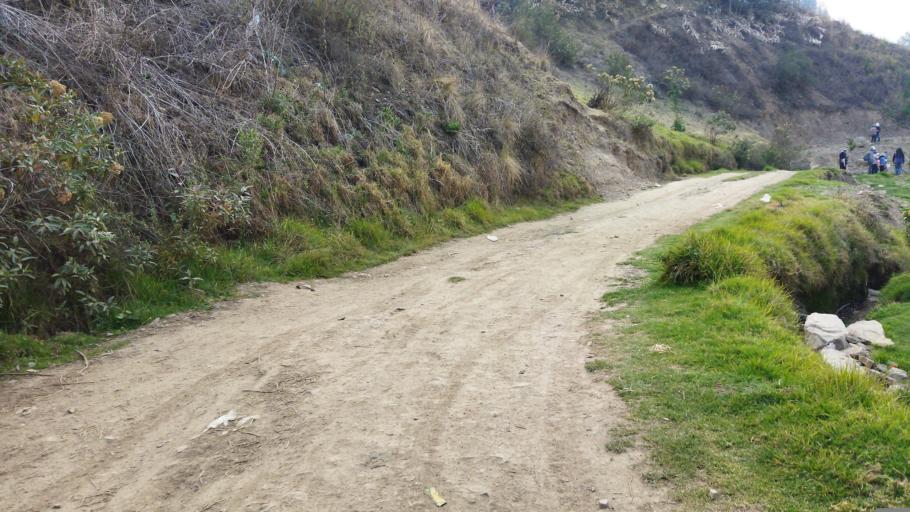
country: BO
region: La Paz
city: Quime
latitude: -16.9852
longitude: -67.1917
